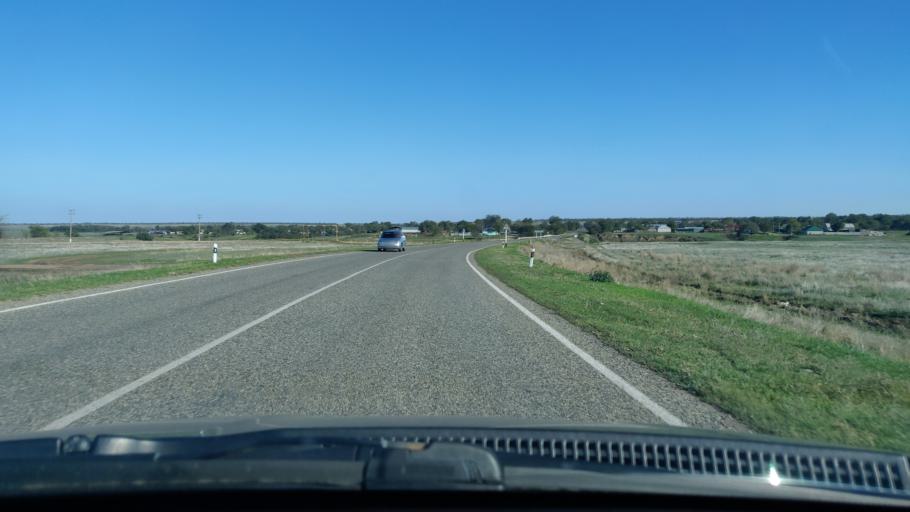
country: RU
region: Stavropol'skiy
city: Letnyaya Stavka
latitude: 45.3777
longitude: 43.6754
